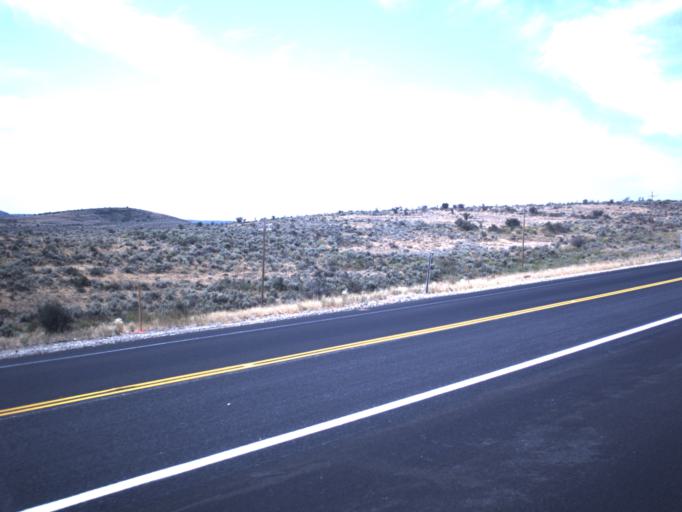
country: US
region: Utah
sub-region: Summit County
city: Kamas
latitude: 40.6397
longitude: -111.3247
